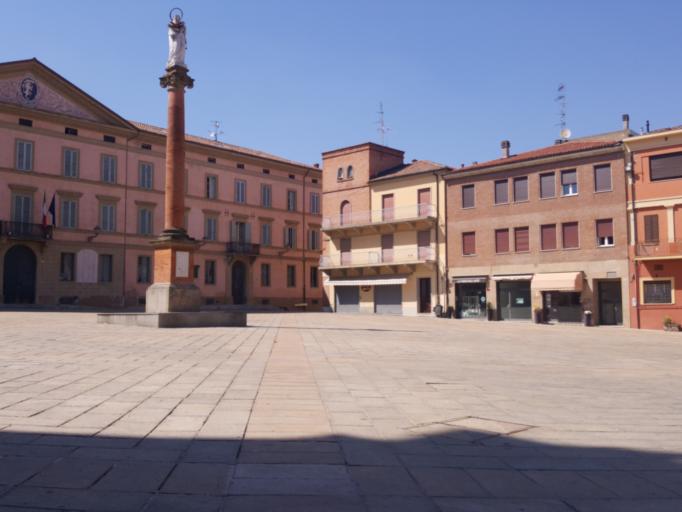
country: IT
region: Emilia-Romagna
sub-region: Provincia di Bologna
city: Castel San Pietro Terme
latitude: 44.3977
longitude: 11.5897
